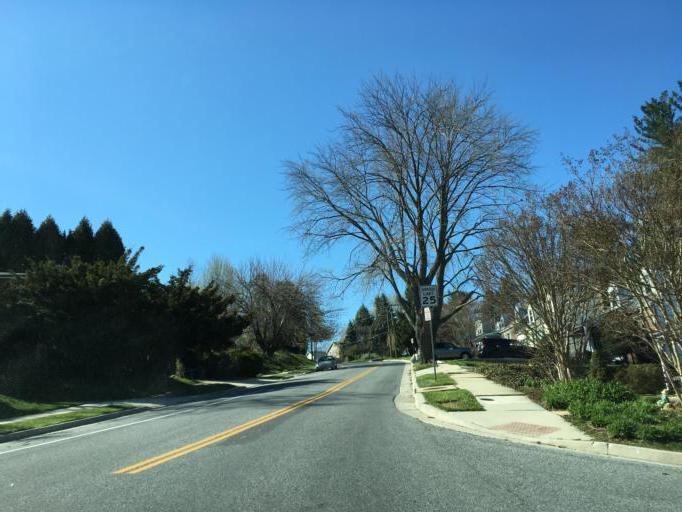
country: US
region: Maryland
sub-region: Baltimore County
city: Towson
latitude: 39.3745
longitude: -76.5868
